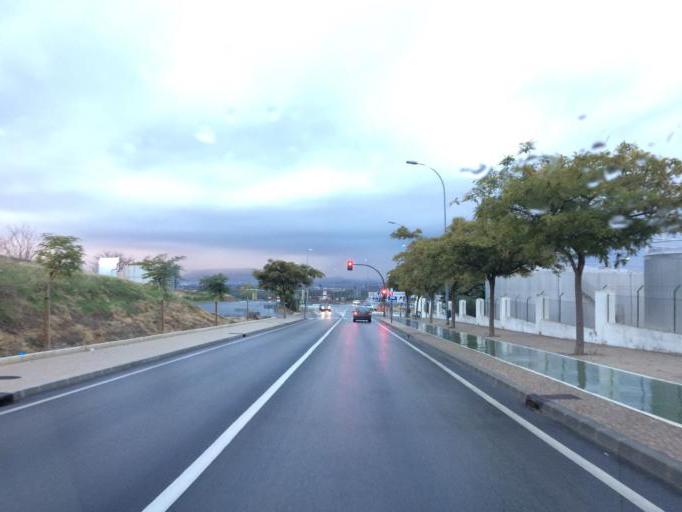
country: ES
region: Andalusia
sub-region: Provincia de Malaga
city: Antequera
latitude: 37.0267
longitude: -4.5628
